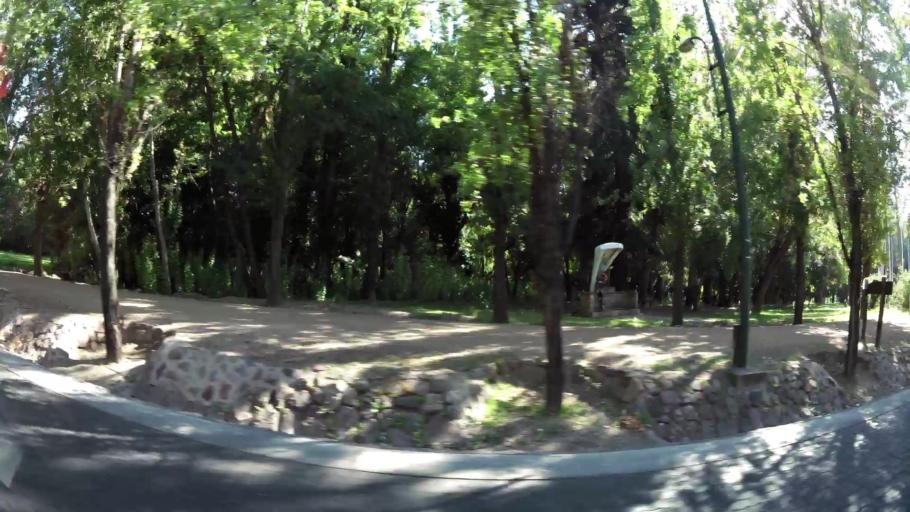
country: AR
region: Mendoza
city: Mendoza
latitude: -32.8861
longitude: -68.8638
